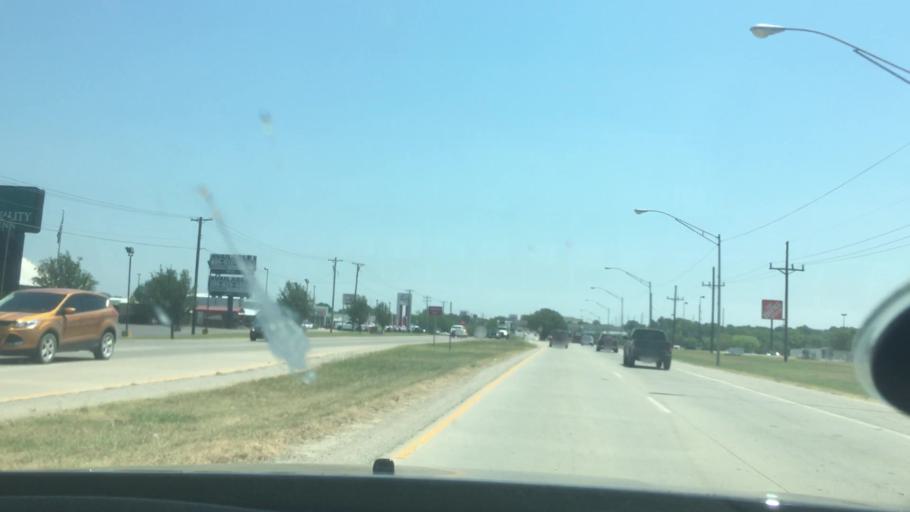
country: US
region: Oklahoma
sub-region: Pontotoc County
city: Ada
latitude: 34.7897
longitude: -96.6748
